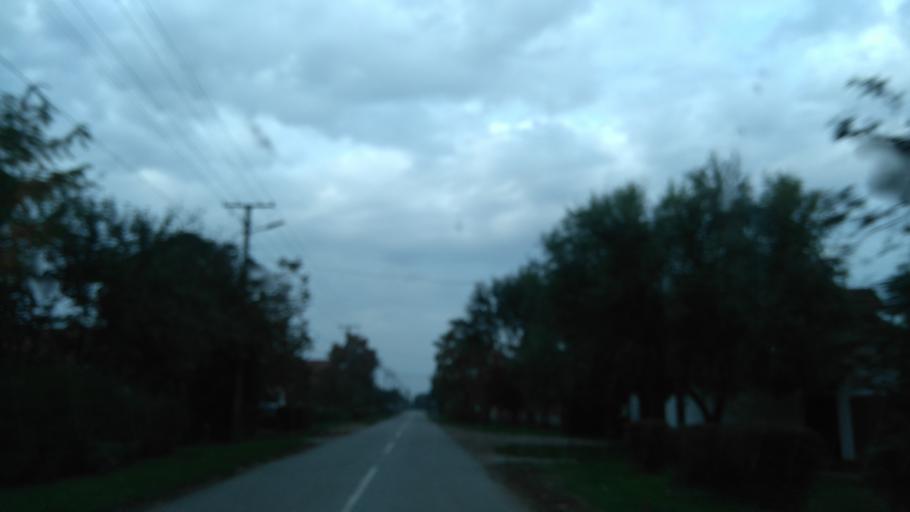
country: RS
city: Mol
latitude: 45.7667
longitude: 20.1359
